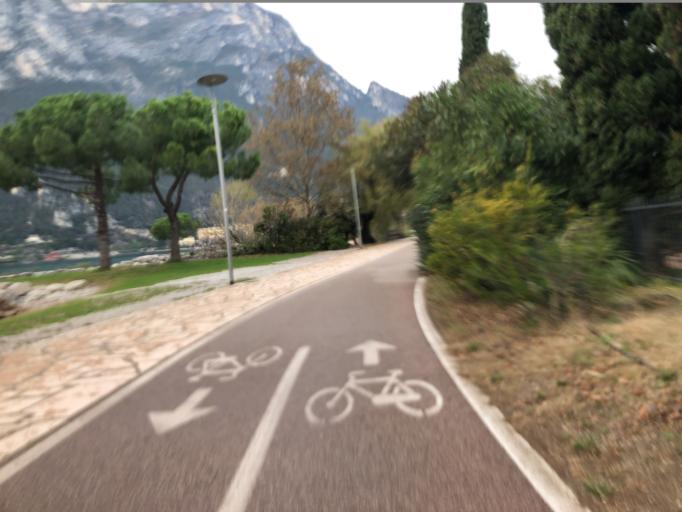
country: IT
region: Trentino-Alto Adige
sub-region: Provincia di Trento
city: Riva del Garda
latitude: 45.8802
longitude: 10.8507
